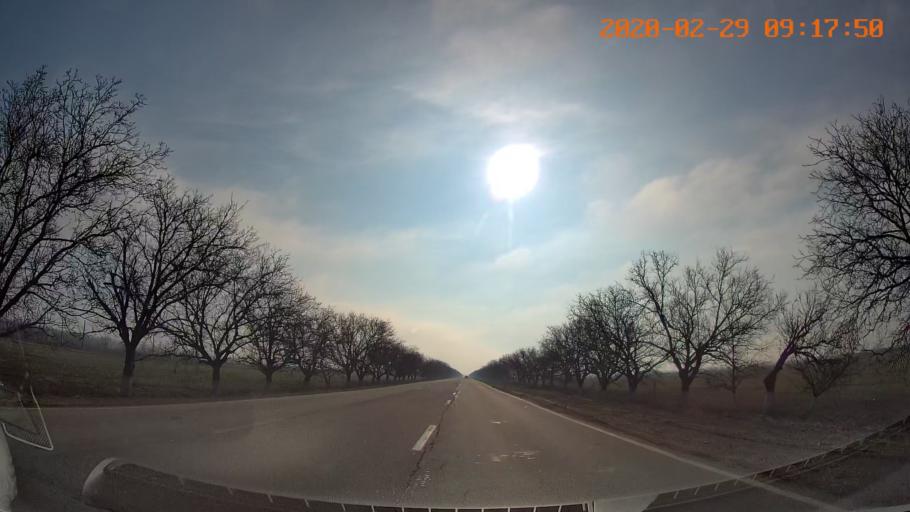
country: MD
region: Telenesti
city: Pervomaisc
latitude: 46.7793
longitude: 29.9116
